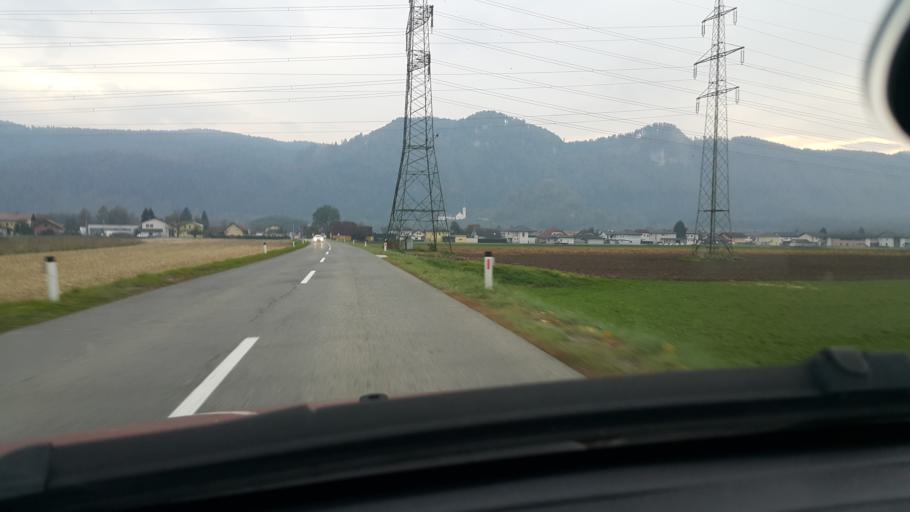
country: AT
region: Carinthia
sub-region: Politischer Bezirk Klagenfurt Land
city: Ebenthal
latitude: 46.6149
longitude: 14.3981
